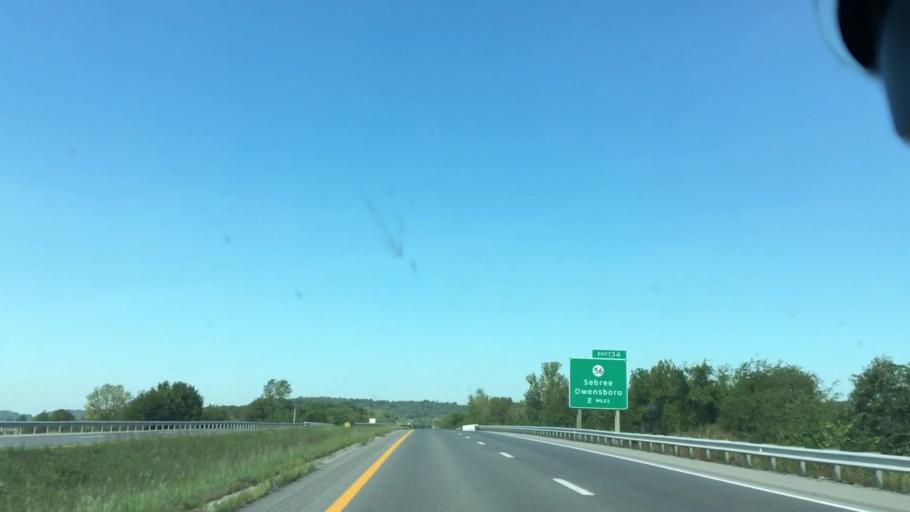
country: US
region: Kentucky
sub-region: Webster County
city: Sebree
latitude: 37.5798
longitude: -87.4838
